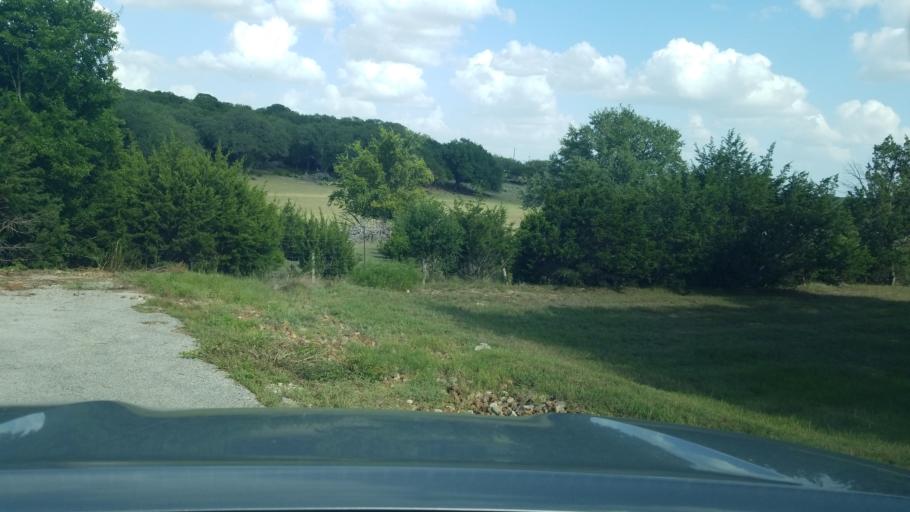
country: US
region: Texas
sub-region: Comal County
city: Bulverde
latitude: 29.8045
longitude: -98.3968
